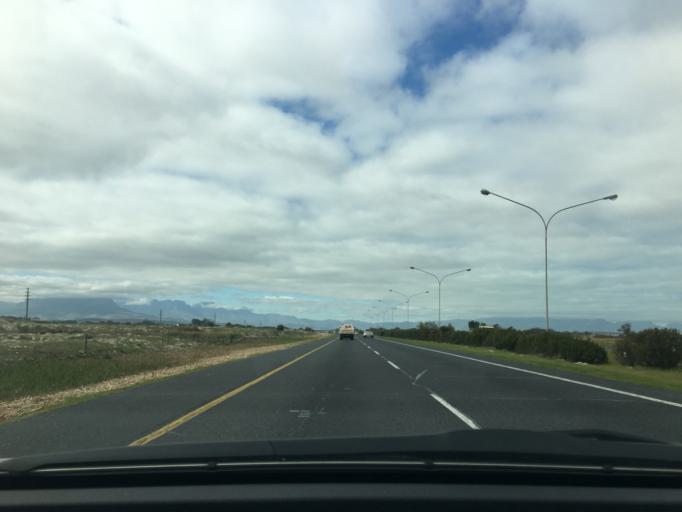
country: ZA
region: Western Cape
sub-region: City of Cape Town
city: Kraaifontein
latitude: -34.0204
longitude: 18.6764
